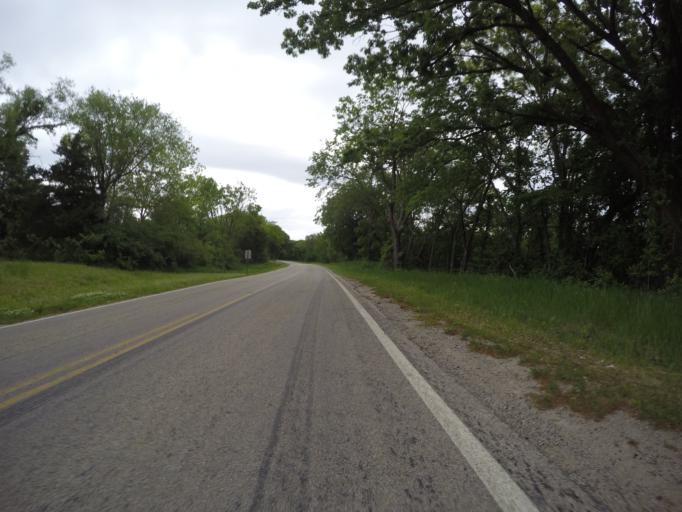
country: US
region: Kansas
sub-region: Pottawatomie County
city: Wamego
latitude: 39.1879
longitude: -96.3294
